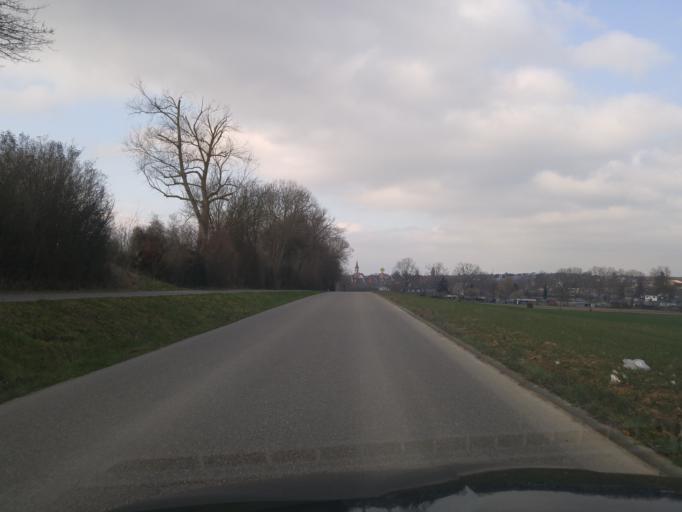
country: DE
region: Baden-Wuerttemberg
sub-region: Regierungsbezirk Stuttgart
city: Ilsfeld
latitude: 49.0530
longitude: 9.2640
